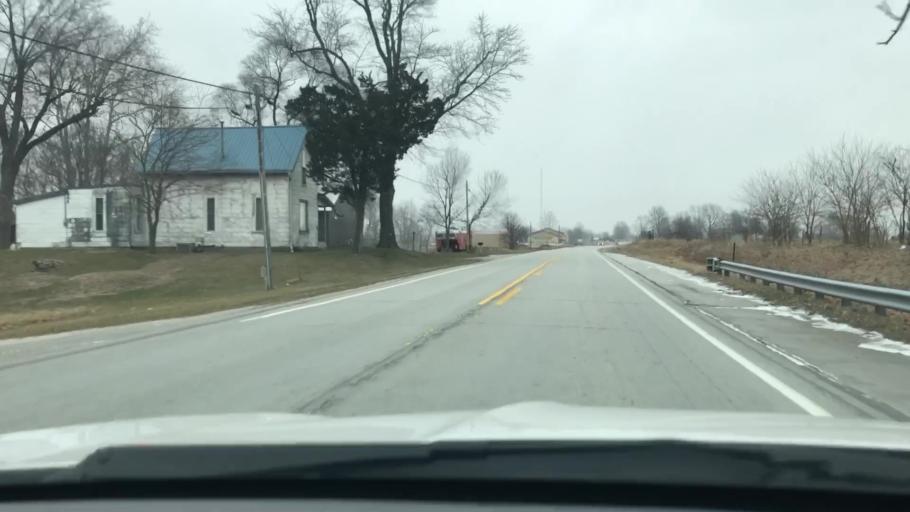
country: US
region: Indiana
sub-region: Fulton County
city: Akron
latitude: 41.0385
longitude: -86.0616
